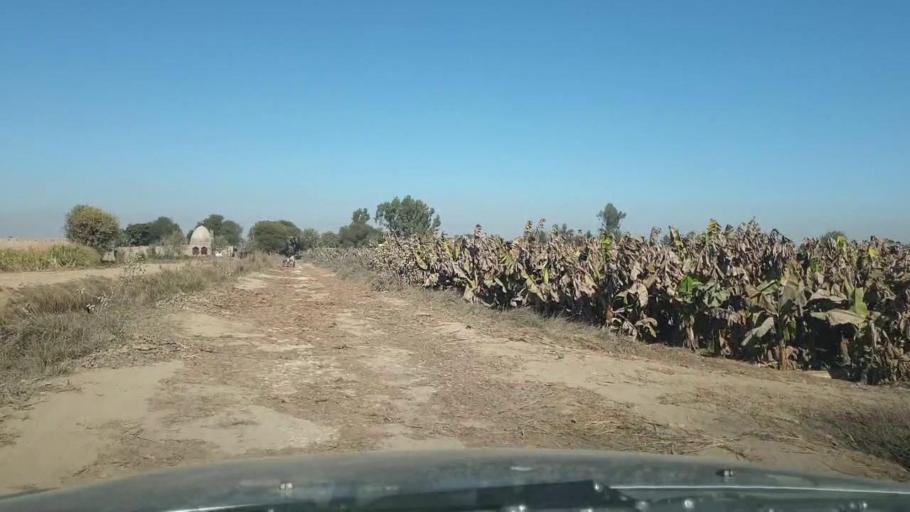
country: PK
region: Sindh
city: Ghotki
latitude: 28.0414
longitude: 69.2467
